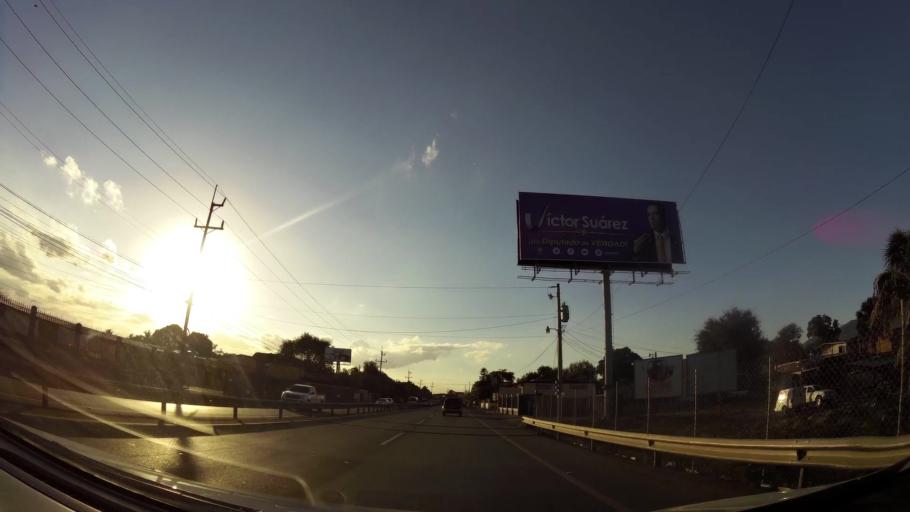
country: DO
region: Santiago
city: Palmar Arriba
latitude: 19.5035
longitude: -70.7493
